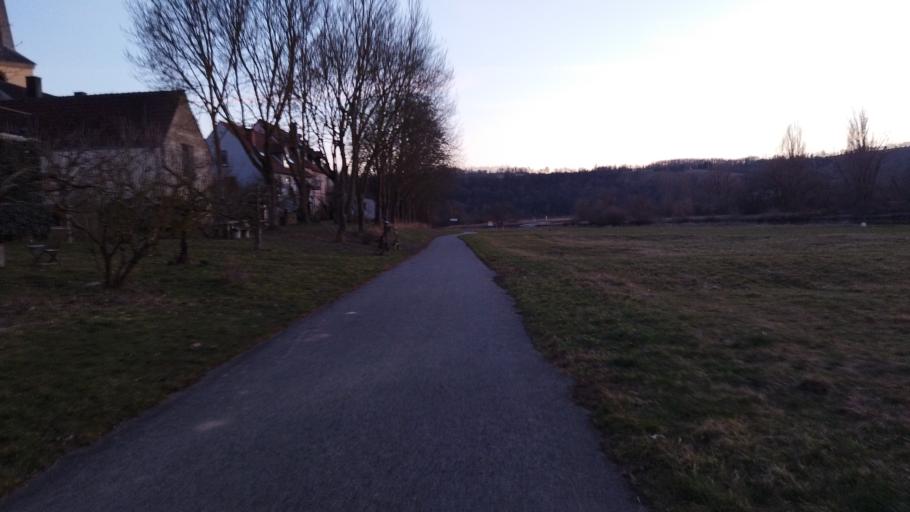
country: DE
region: Bavaria
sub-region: Regierungsbezirk Unterfranken
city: Nordheim
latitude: 49.8780
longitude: 10.1649
